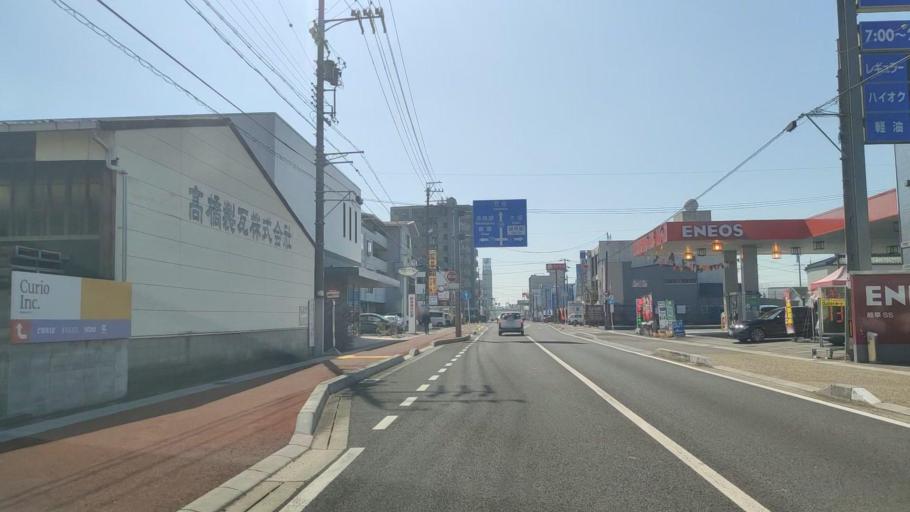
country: JP
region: Gifu
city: Gifu-shi
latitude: 35.3988
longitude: 136.7657
